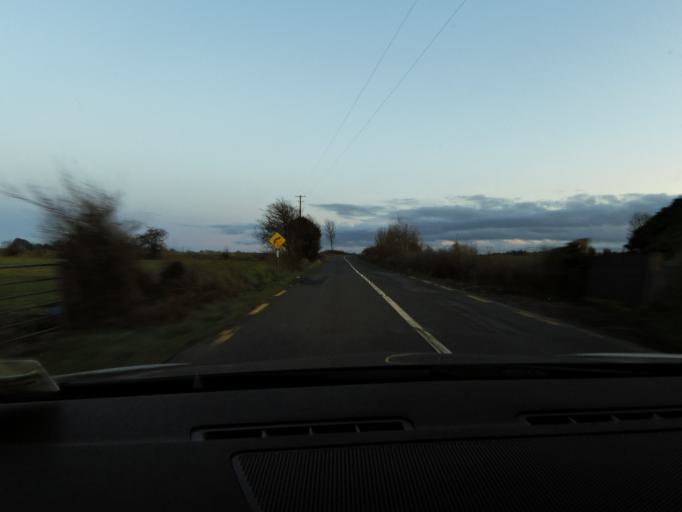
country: IE
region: Connaught
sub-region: Roscommon
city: Boyle
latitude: 53.8507
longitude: -8.2273
